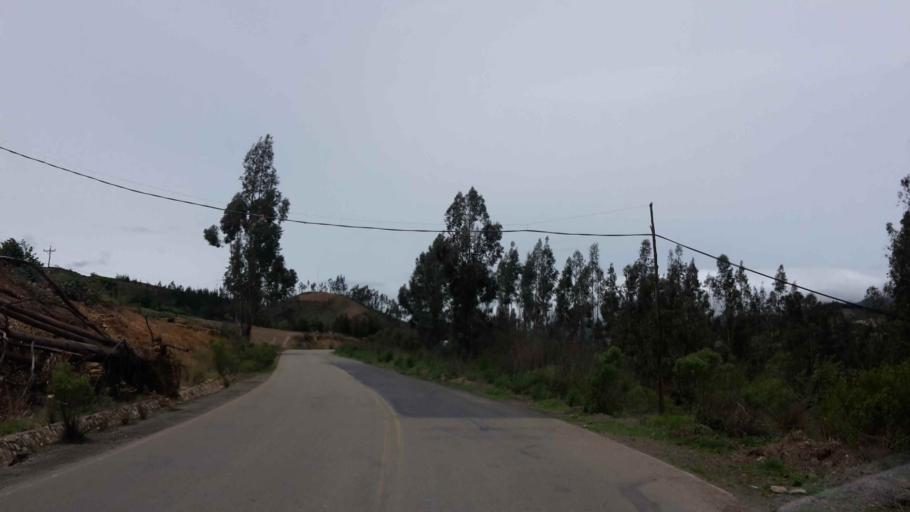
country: BO
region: Cochabamba
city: Totora
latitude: -17.6900
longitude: -65.2145
